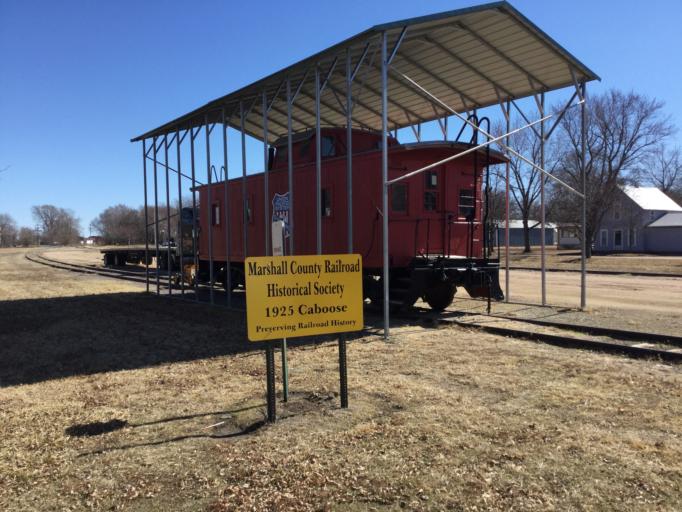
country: US
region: Kansas
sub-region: Marshall County
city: Blue Rapids
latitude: 39.6914
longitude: -96.7475
